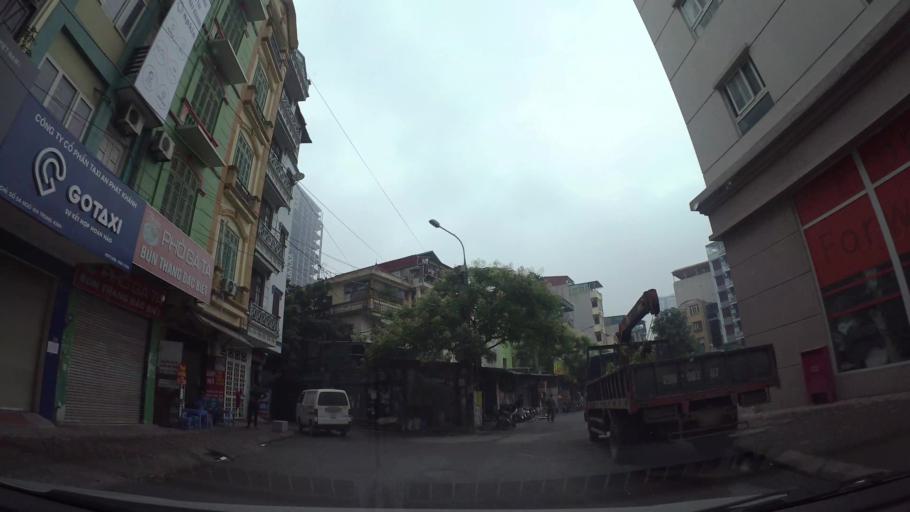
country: VN
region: Ha Noi
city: Cau Giay
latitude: 21.0205
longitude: 105.7925
